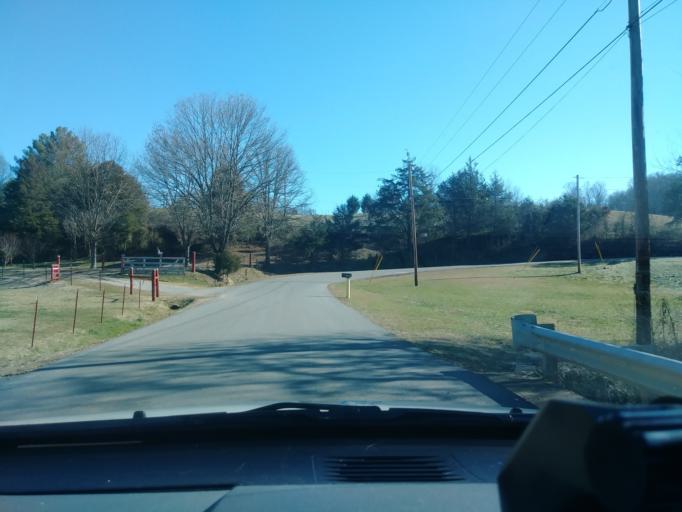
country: US
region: Tennessee
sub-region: Greene County
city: Mosheim
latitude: 36.1053
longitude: -82.9102
